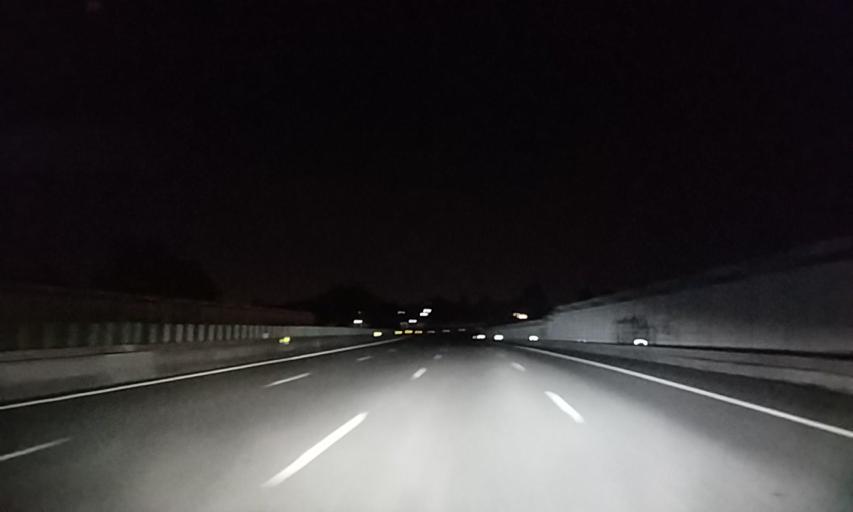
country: PT
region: Porto
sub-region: Vila Nova de Gaia
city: Grijo
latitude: 41.0310
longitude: -8.5718
